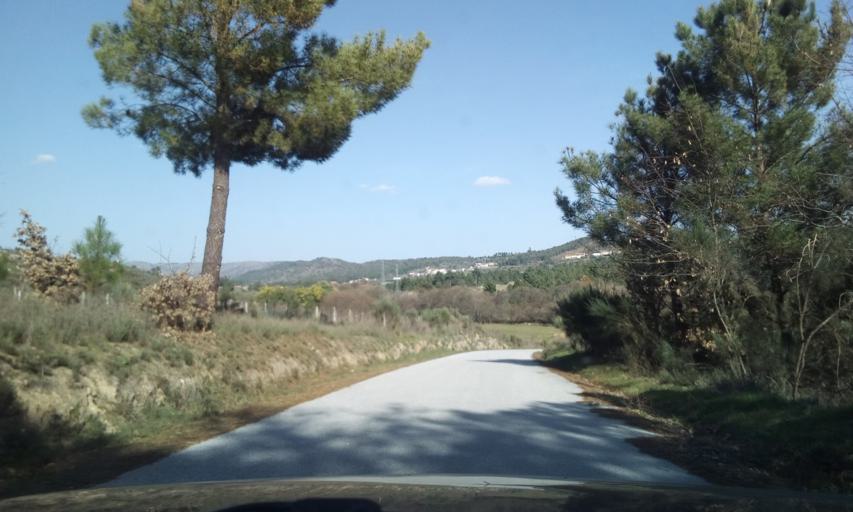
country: PT
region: Guarda
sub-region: Celorico da Beira
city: Celorico da Beira
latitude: 40.6493
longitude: -7.4260
